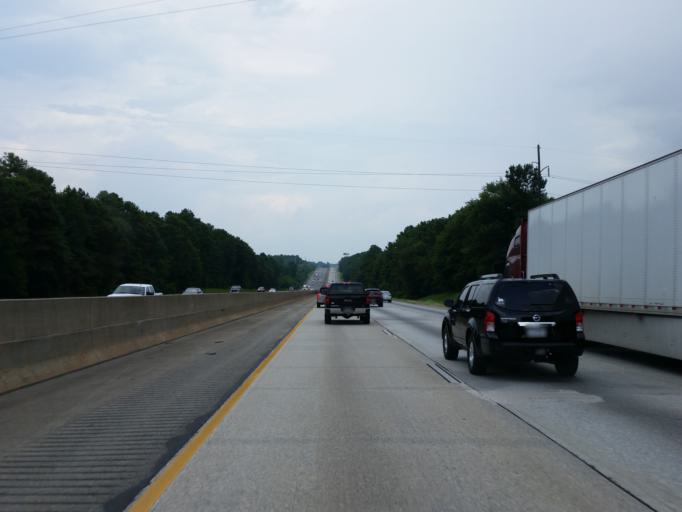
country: US
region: Georgia
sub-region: Monroe County
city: Forsyth
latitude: 33.0116
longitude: -83.8795
